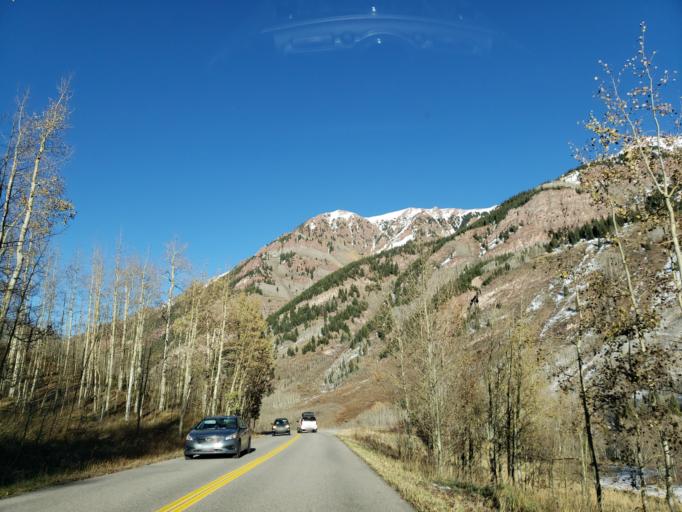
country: US
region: Colorado
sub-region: Pitkin County
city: Snowmass Village
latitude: 39.1104
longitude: -106.9148
